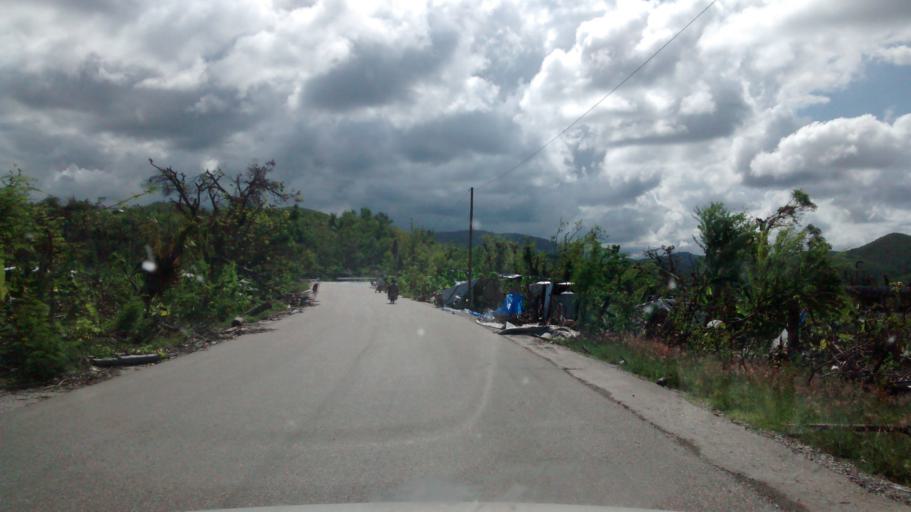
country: HT
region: Grandans
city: Jeremie
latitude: 18.6125
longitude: -74.0759
